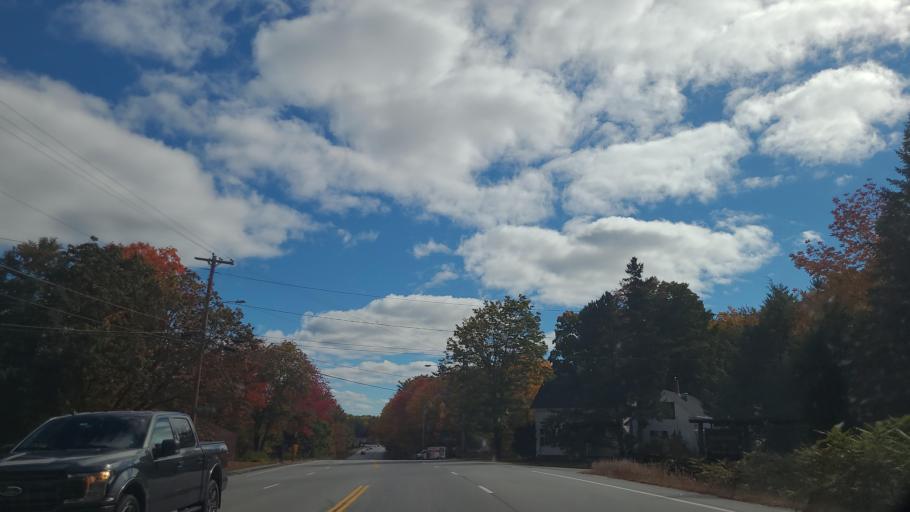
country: US
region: Maine
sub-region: Cumberland County
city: Raymond
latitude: 43.9139
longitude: -70.5184
